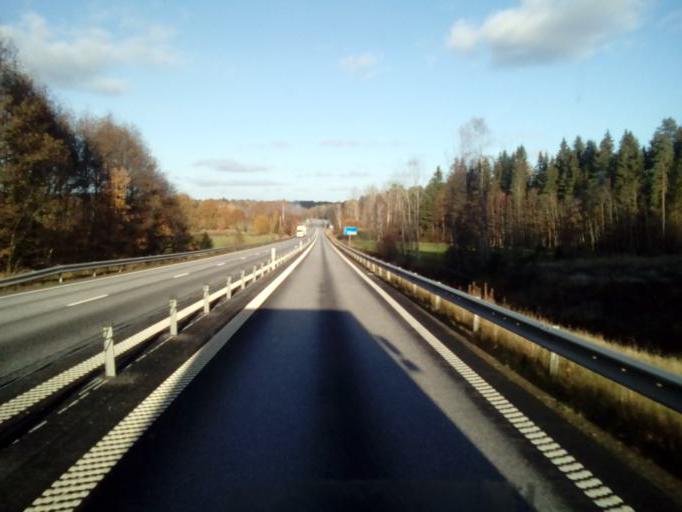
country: SE
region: Kalmar
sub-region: Vimmerby Kommun
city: Vimmerby
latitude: 57.6868
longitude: 15.9986
